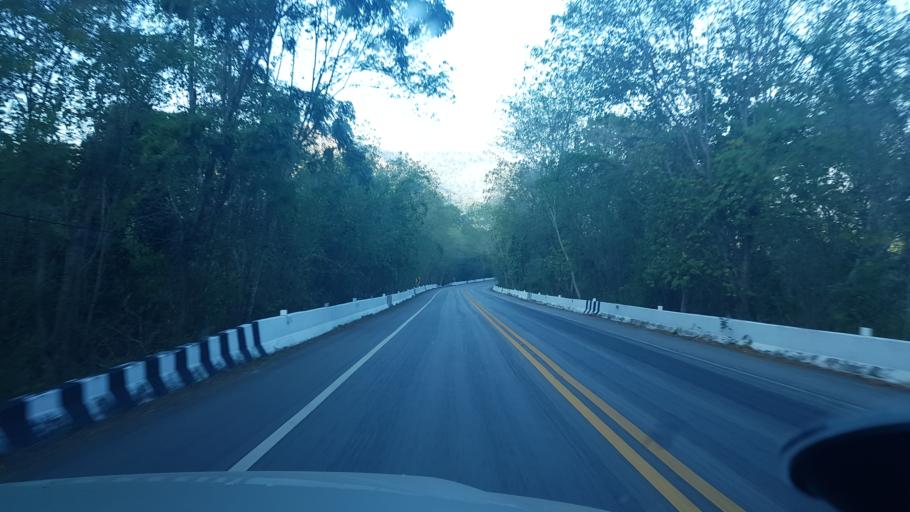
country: TH
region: Khon Kaen
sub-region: Amphoe Phu Pha Man
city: Phu Pha Man
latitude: 16.6472
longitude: 101.7853
